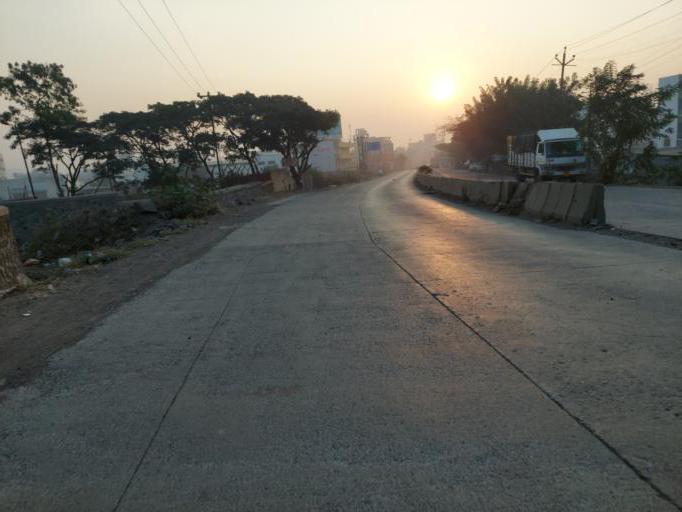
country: IN
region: Maharashtra
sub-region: Pune Division
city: Pune
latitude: 18.4663
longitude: 73.9591
